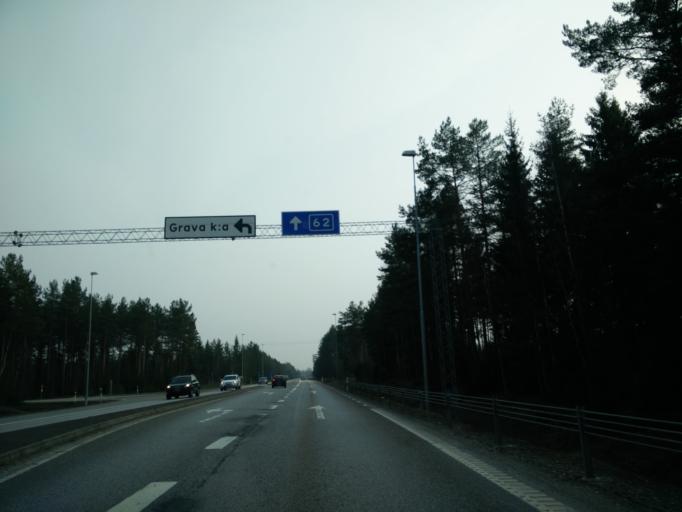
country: SE
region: Vaermland
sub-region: Forshaga Kommun
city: Forshaga
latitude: 59.4560
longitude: 13.4166
